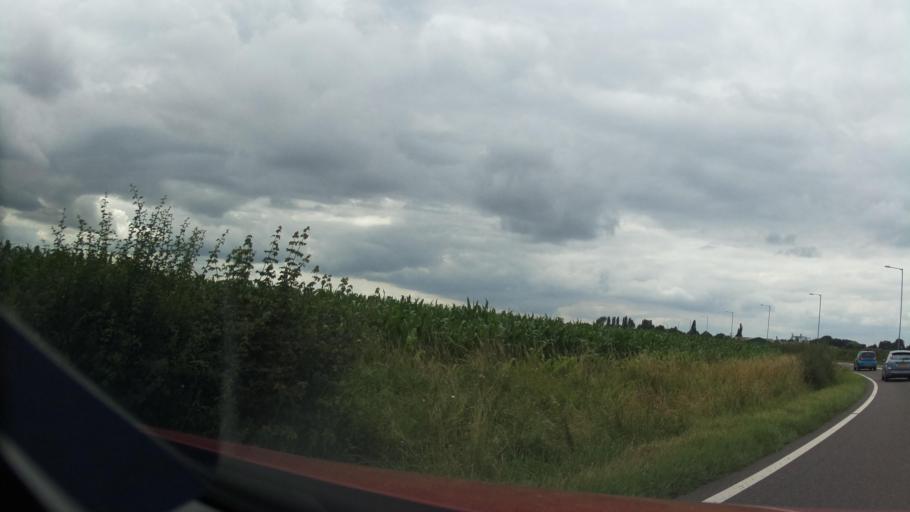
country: GB
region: England
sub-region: Lincolnshire
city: Barrowby
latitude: 52.9294
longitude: -0.7136
